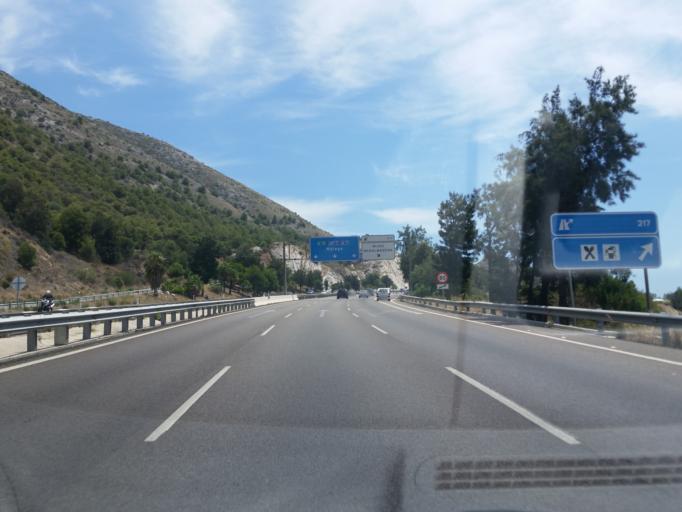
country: ES
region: Andalusia
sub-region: Provincia de Malaga
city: Benalmadena
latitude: 36.5863
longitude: -4.5993
